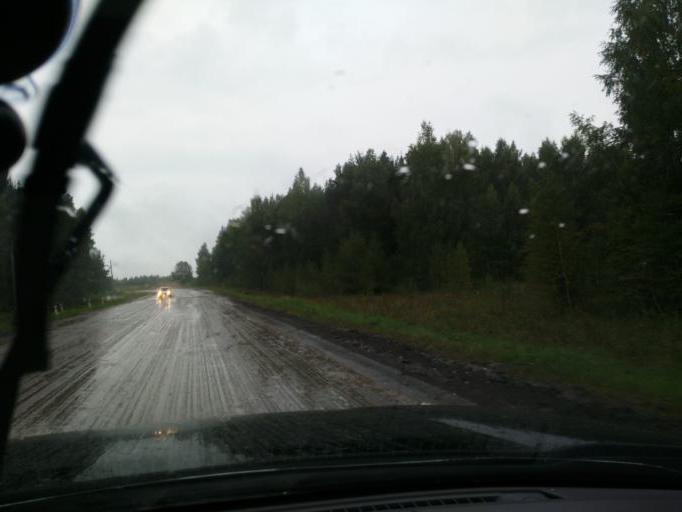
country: RU
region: Perm
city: Osa
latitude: 57.3221
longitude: 55.6156
